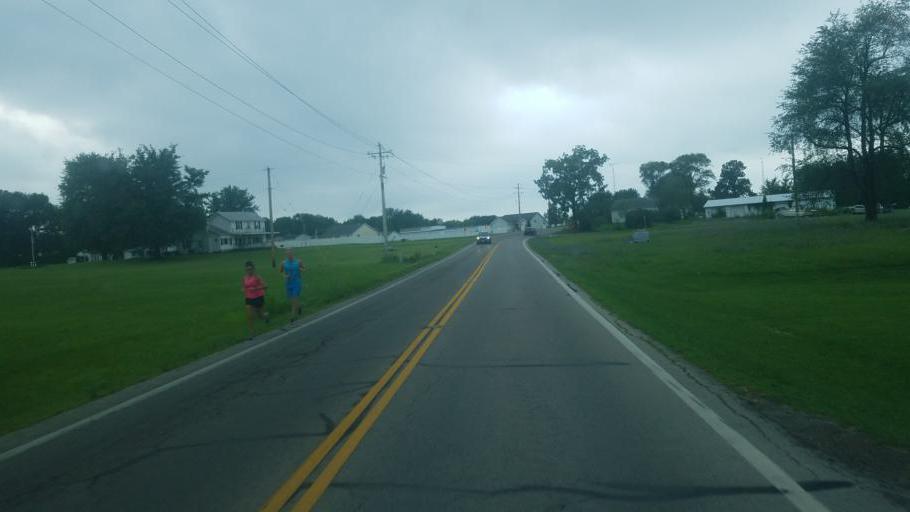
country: US
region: Ohio
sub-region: Logan County
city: Russells Point
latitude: 40.5261
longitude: -83.8575
